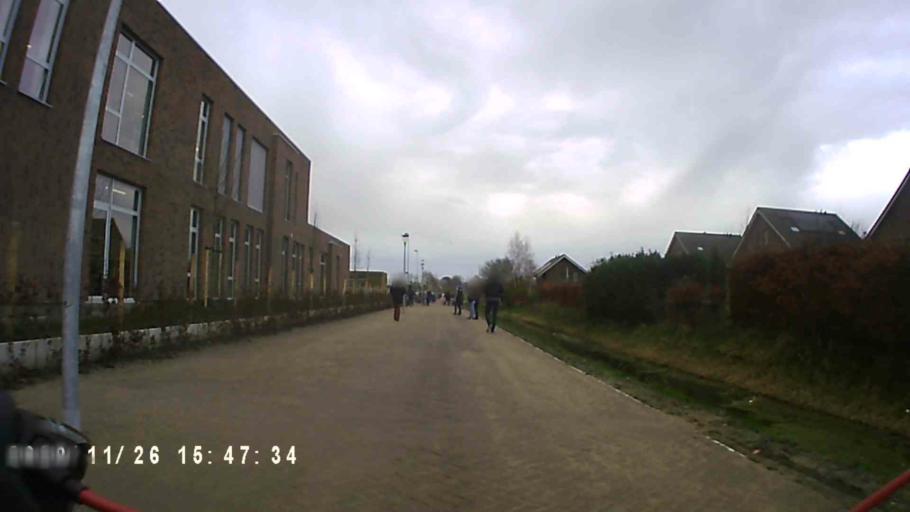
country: NL
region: Groningen
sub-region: Gemeente Bedum
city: Bedum
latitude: 53.2799
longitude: 6.7051
